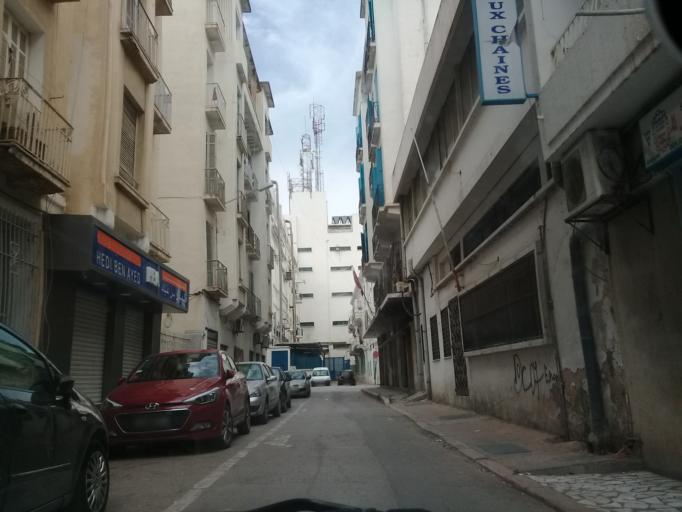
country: TN
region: Tunis
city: Tunis
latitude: 36.7972
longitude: 10.1834
